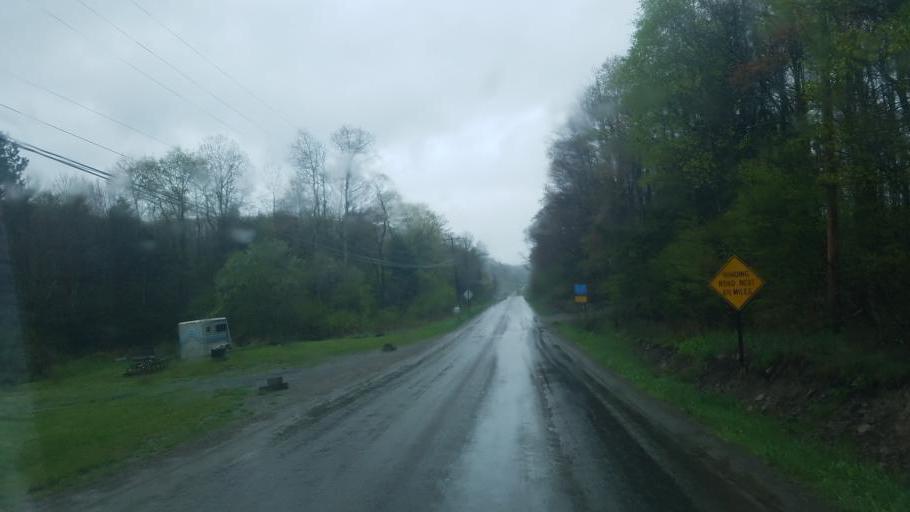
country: US
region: New York
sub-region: Allegany County
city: Andover
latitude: 41.9228
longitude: -77.7810
